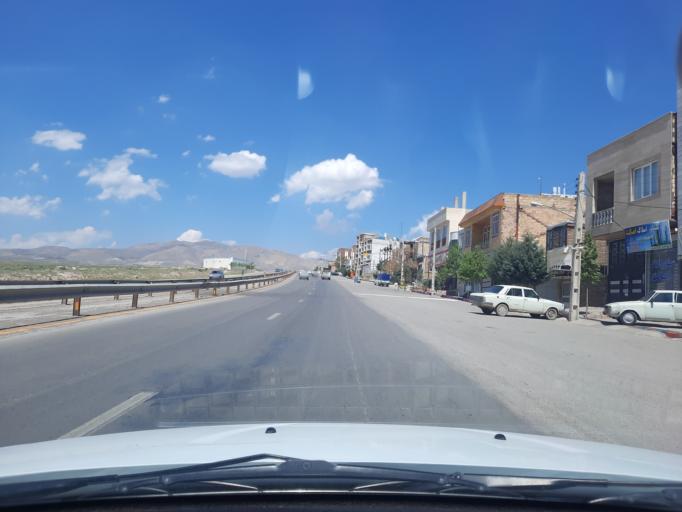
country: IR
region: Qazvin
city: Alvand
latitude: 36.2886
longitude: 50.1333
